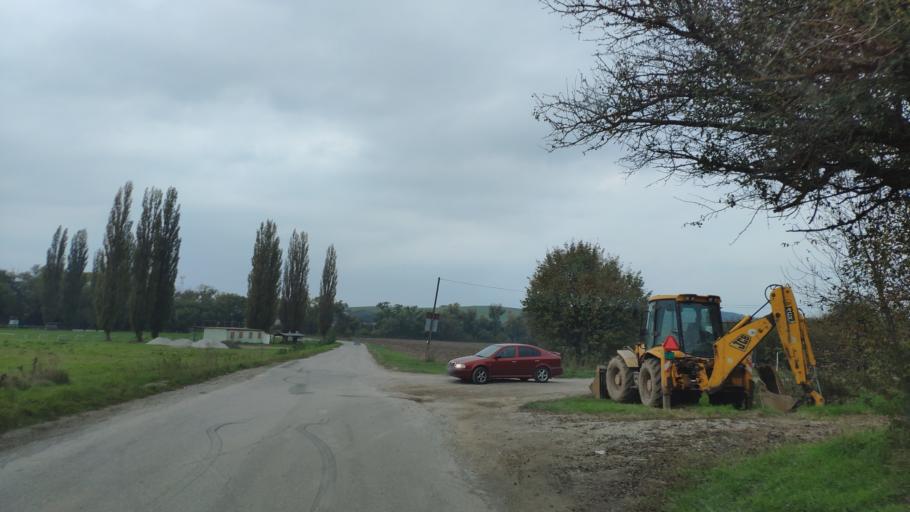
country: SK
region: Kosicky
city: Kosice
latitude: 48.6369
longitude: 21.3798
